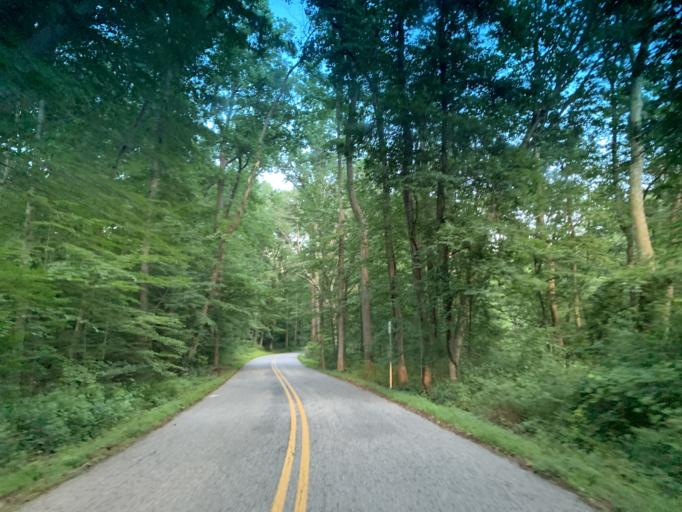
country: US
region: Maryland
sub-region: Harford County
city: Aberdeen
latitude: 39.5346
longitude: -76.1618
